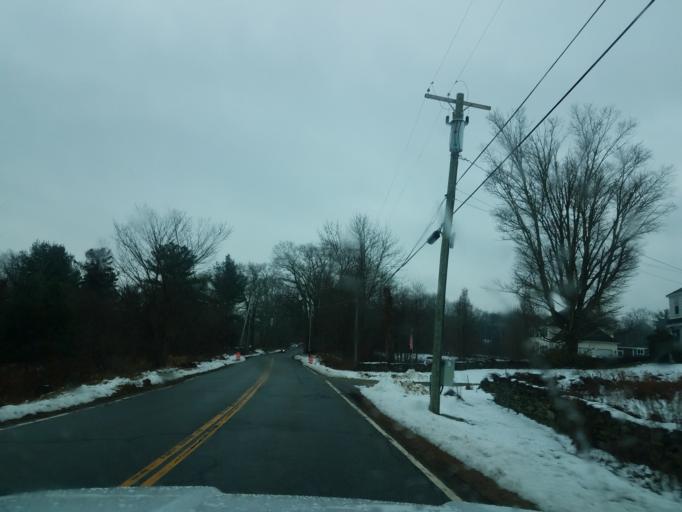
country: US
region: Connecticut
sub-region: Windham County
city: Quinebaug
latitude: 42.0047
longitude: -72.0010
